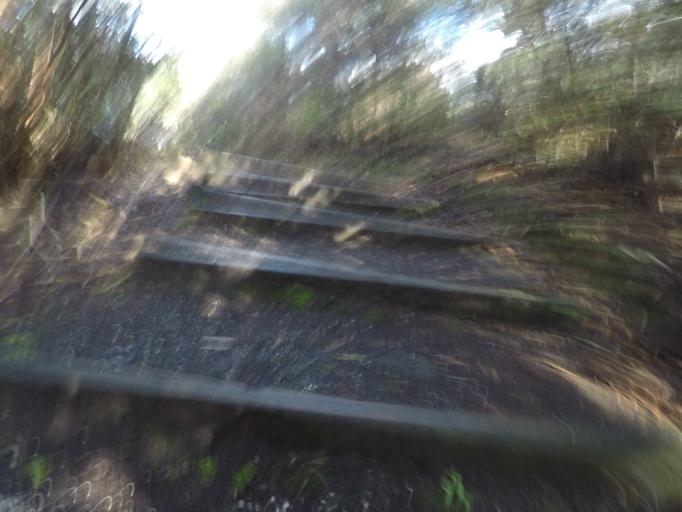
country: NZ
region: Auckland
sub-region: Auckland
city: Waitakere
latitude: -36.9010
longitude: 174.6432
